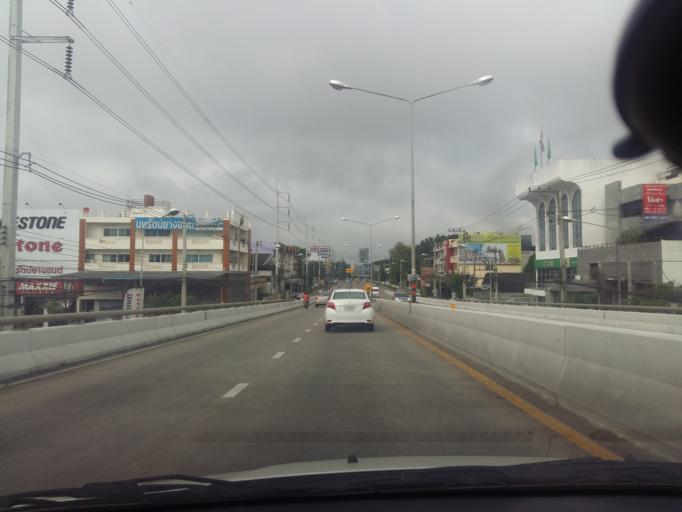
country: TH
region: Chiang Mai
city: Chiang Mai
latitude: 18.7584
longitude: 99.0014
